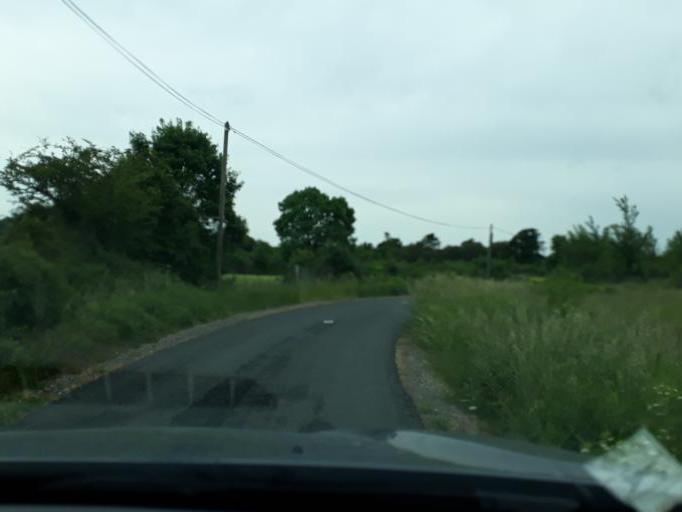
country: FR
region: Languedoc-Roussillon
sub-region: Departement de l'Herault
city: Lodeve
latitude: 43.8355
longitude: 3.2780
